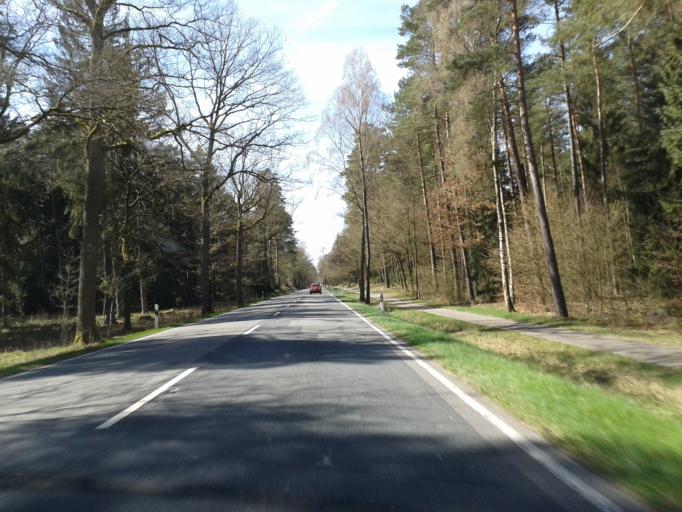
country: DE
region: Lower Saxony
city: Fassberg
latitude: 52.9691
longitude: 10.1998
